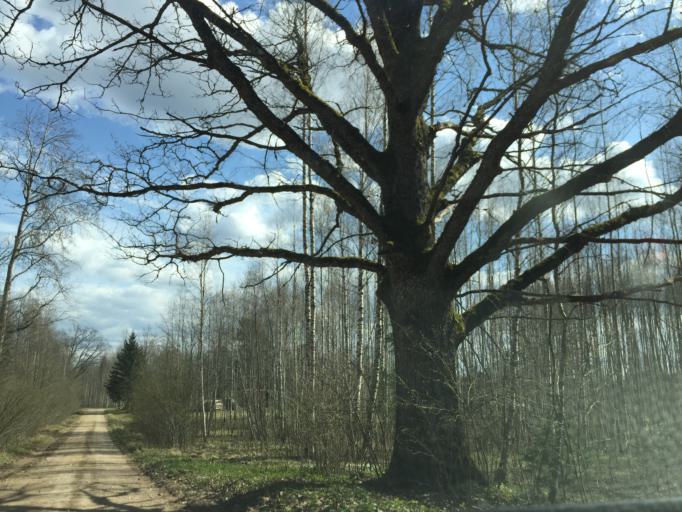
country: LV
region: Skriveri
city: Skriveri
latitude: 56.7982
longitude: 25.1646
